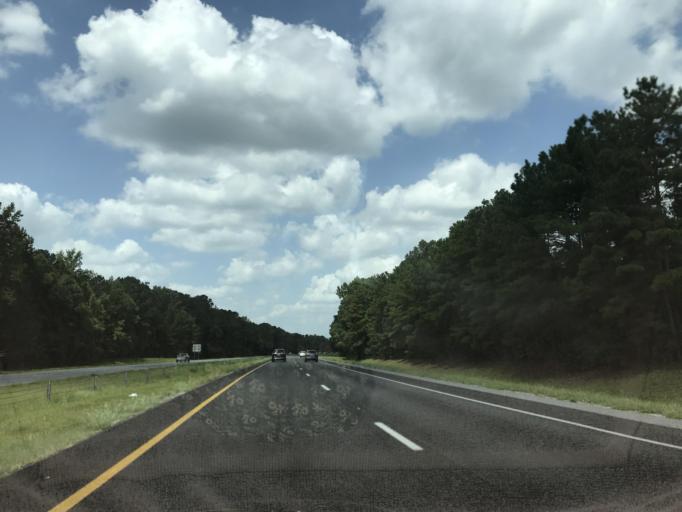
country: US
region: North Carolina
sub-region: Duplin County
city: Rose Hill
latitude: 34.7961
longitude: -77.9834
